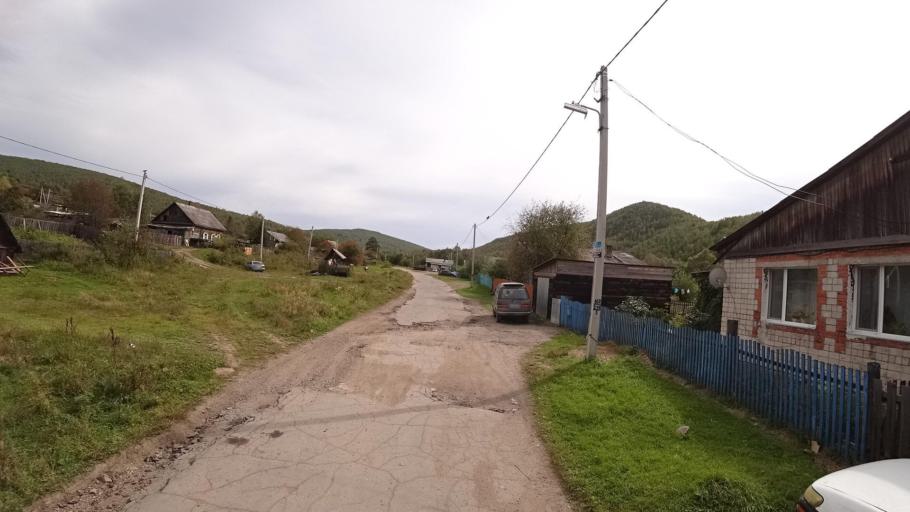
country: RU
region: Jewish Autonomous Oblast
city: Khingansk
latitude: 49.1228
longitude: 131.2047
